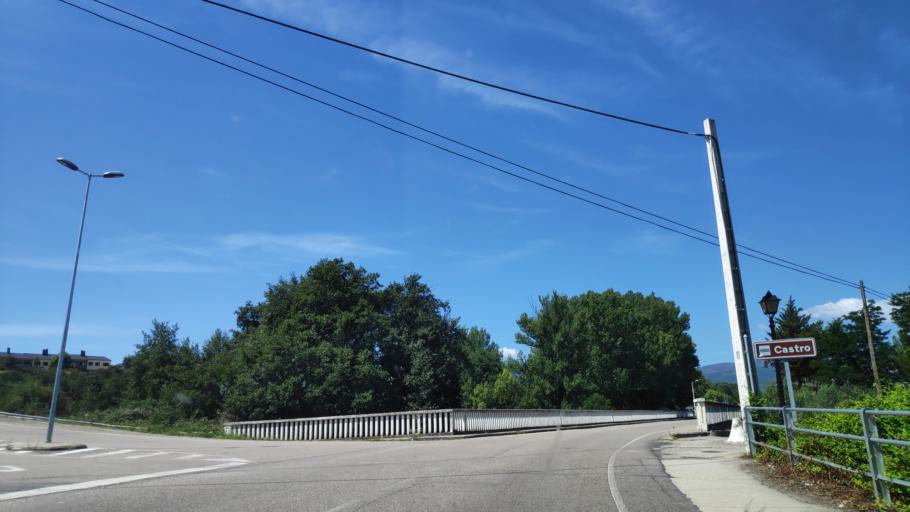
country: ES
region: Castille and Leon
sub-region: Provincia de Zamora
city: Puebla de Sanabria
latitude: 42.0559
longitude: -6.6369
